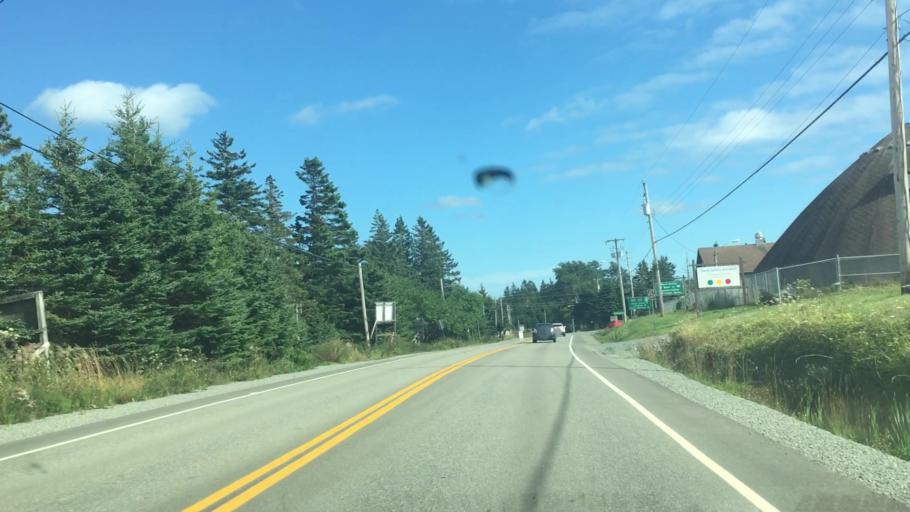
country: CA
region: Nova Scotia
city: Princeville
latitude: 45.6525
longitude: -60.8591
